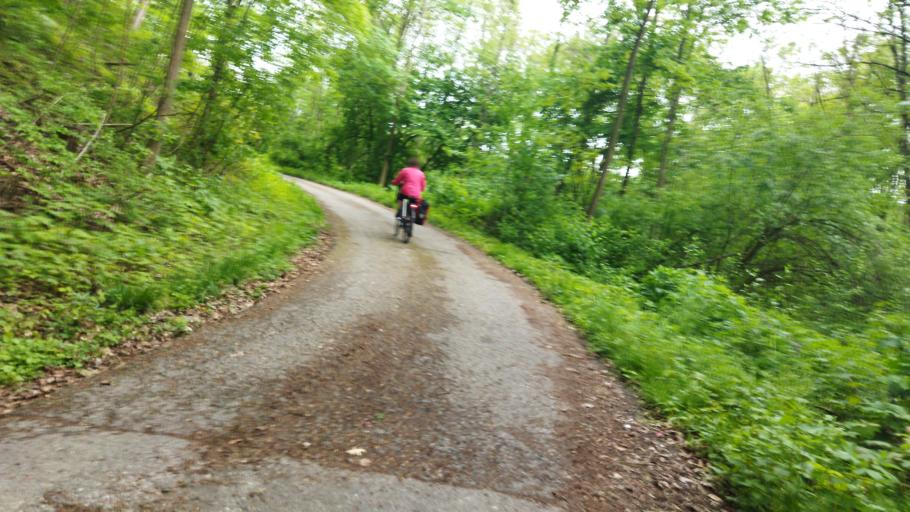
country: DE
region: Baden-Wuerttemberg
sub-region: Regierungsbezirk Stuttgart
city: Neckarwestheim
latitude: 49.0340
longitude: 9.1773
